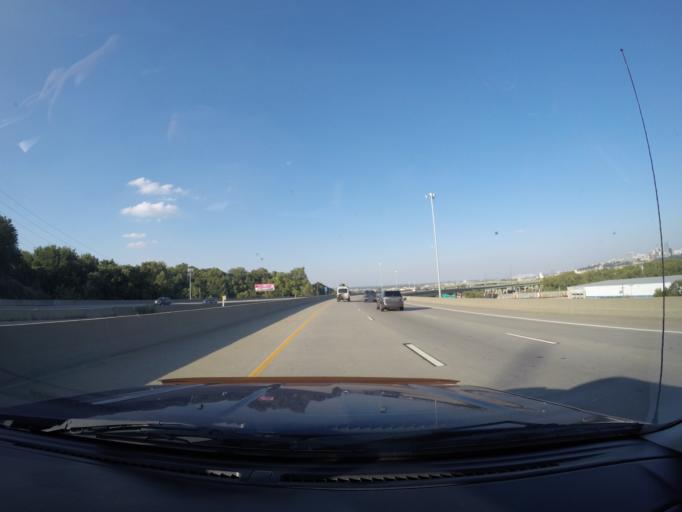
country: US
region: Kansas
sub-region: Wyandotte County
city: Kansas City
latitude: 39.0976
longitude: -94.6244
